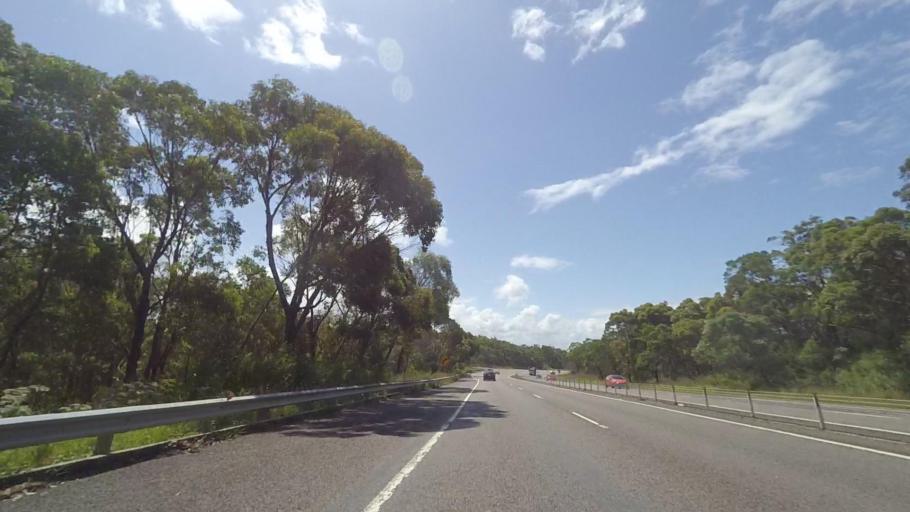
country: AU
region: New South Wales
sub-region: Wyong Shire
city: Kingfisher Shores
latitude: -33.1448
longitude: 151.6116
